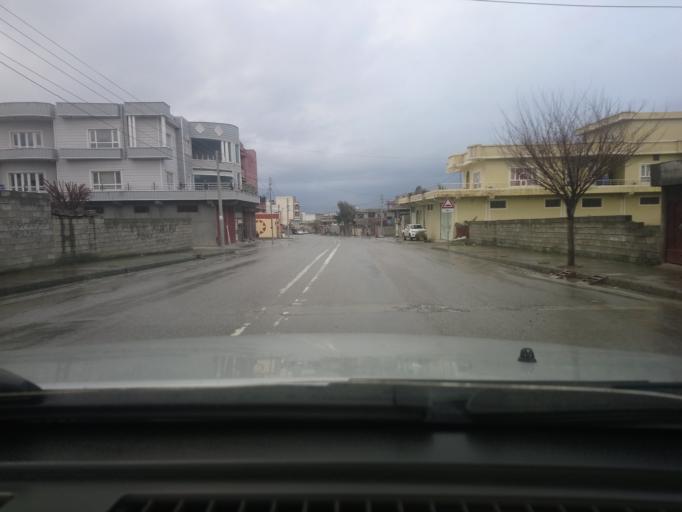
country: IQ
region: As Sulaymaniyah
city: Qeladize
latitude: 36.1784
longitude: 45.1413
